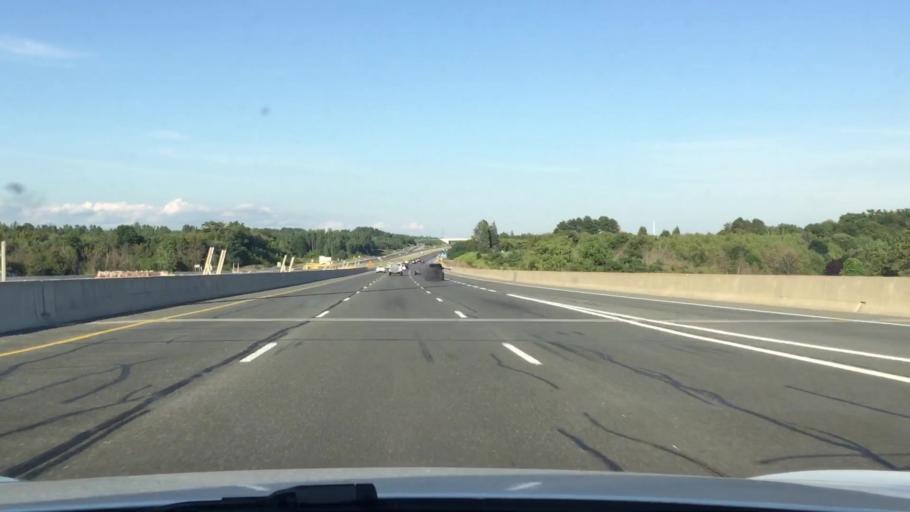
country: CA
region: Ontario
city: Markham
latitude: 43.8650
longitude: -79.2526
